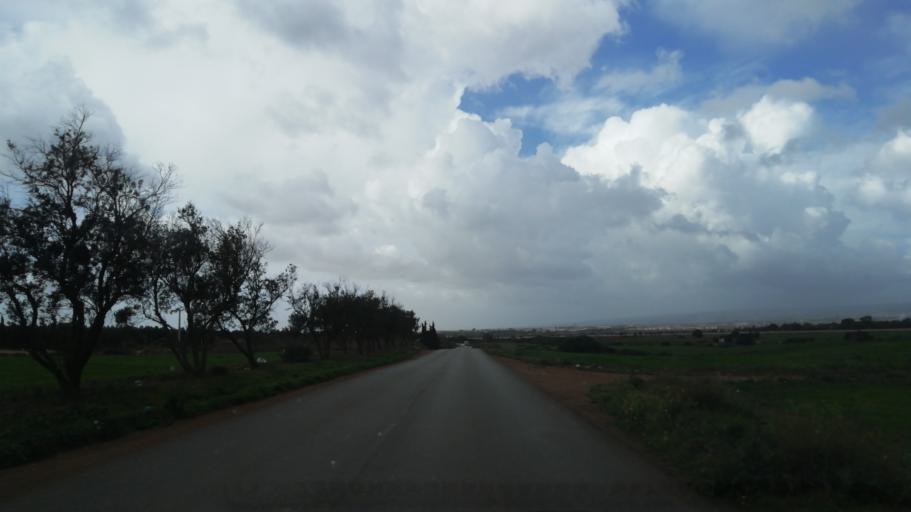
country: DZ
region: Oran
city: Sidi ech Chahmi
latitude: 35.6252
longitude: -0.5405
